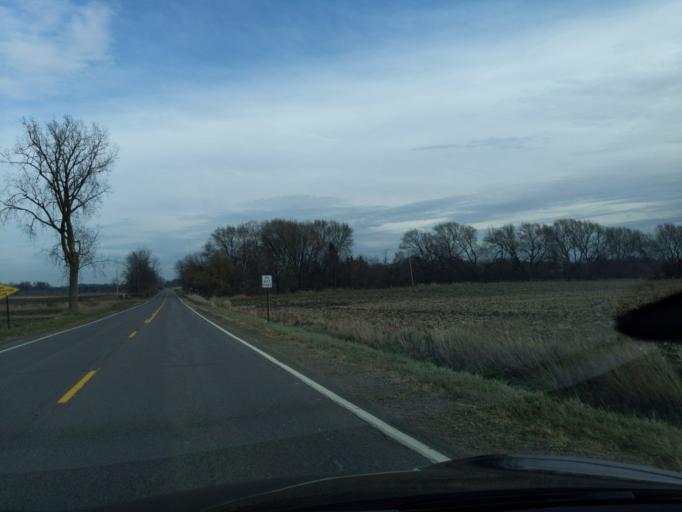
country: US
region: Michigan
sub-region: Ingham County
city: Mason
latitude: 42.6401
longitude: -84.4150
